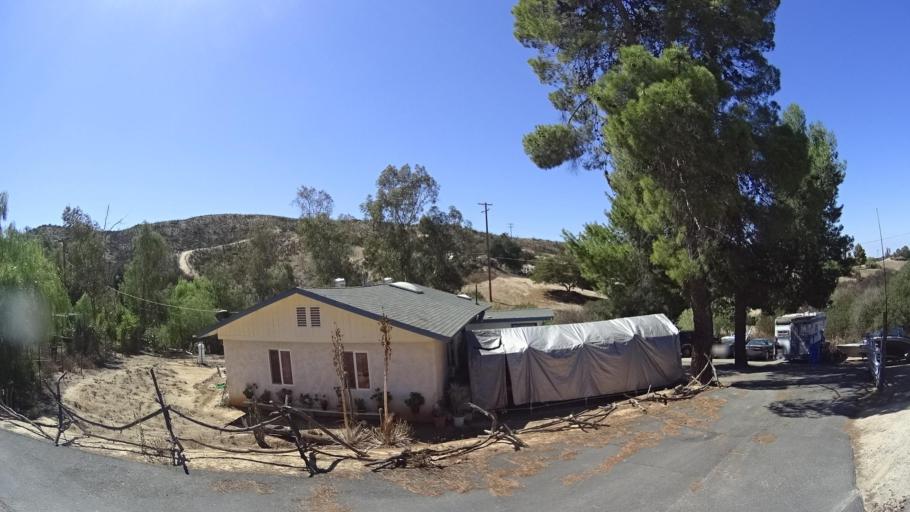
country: US
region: California
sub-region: San Diego County
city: Alpine
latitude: 32.7722
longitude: -116.7700
